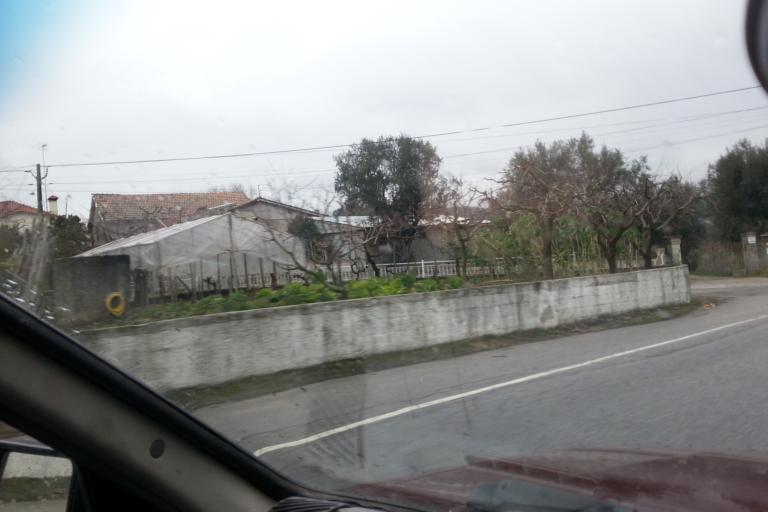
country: PT
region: Viseu
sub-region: Viseu
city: Rio de Loba
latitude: 40.6399
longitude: -7.8346
